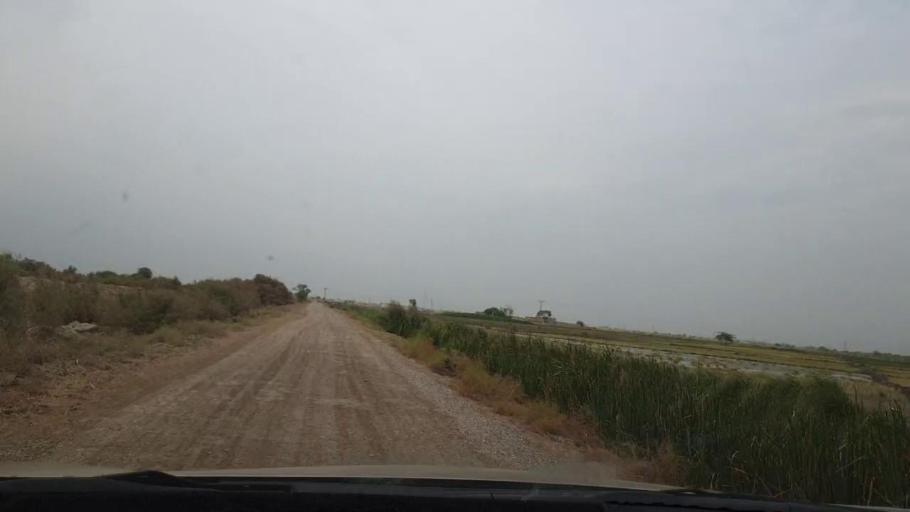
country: PK
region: Sindh
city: Ratodero
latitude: 27.7724
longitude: 68.2765
